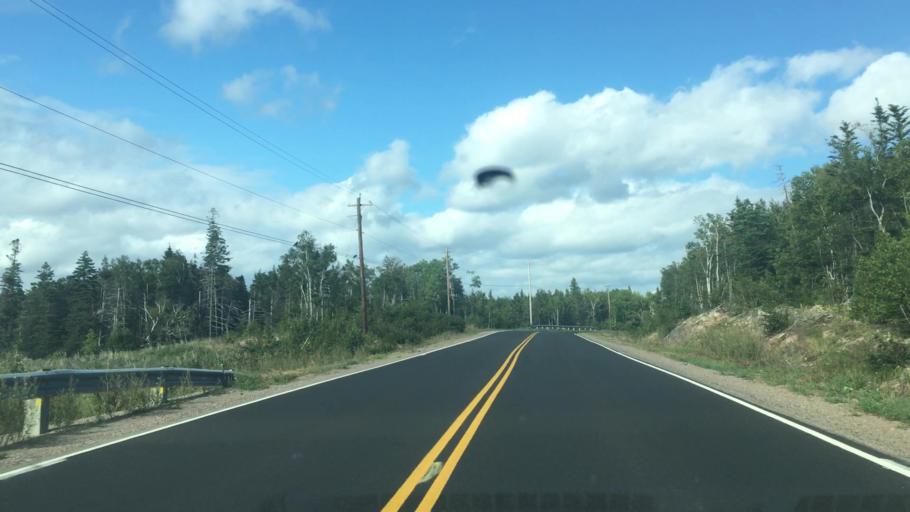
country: CA
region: Nova Scotia
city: Princeville
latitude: 45.8099
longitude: -60.7073
